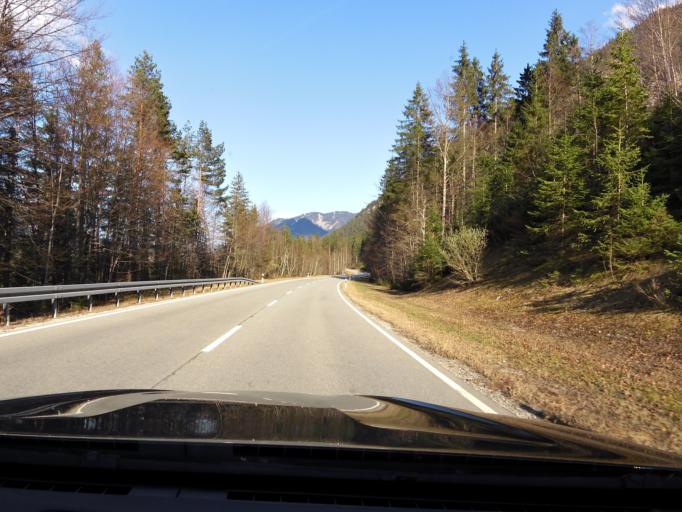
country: DE
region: Bavaria
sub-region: Upper Bavaria
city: Jachenau
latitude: 47.5586
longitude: 11.4786
